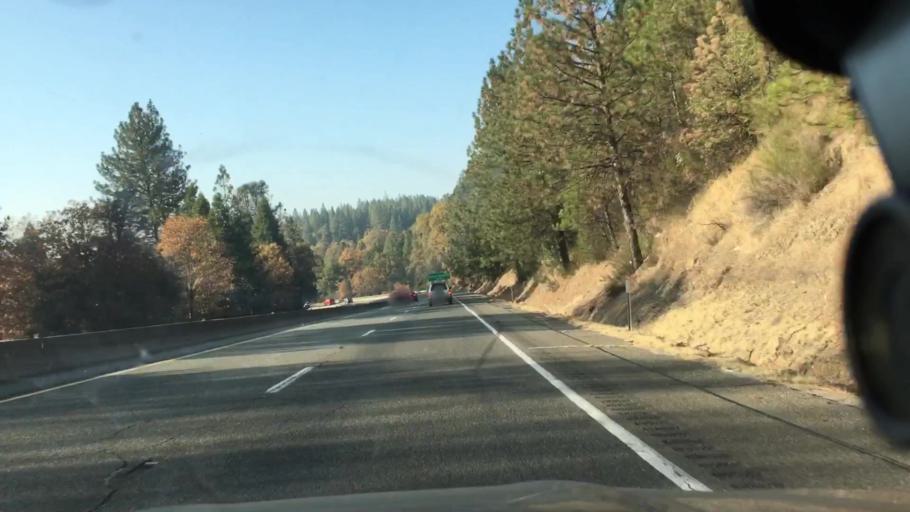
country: US
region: California
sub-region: El Dorado County
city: Placerville
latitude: 38.7317
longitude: -120.7687
